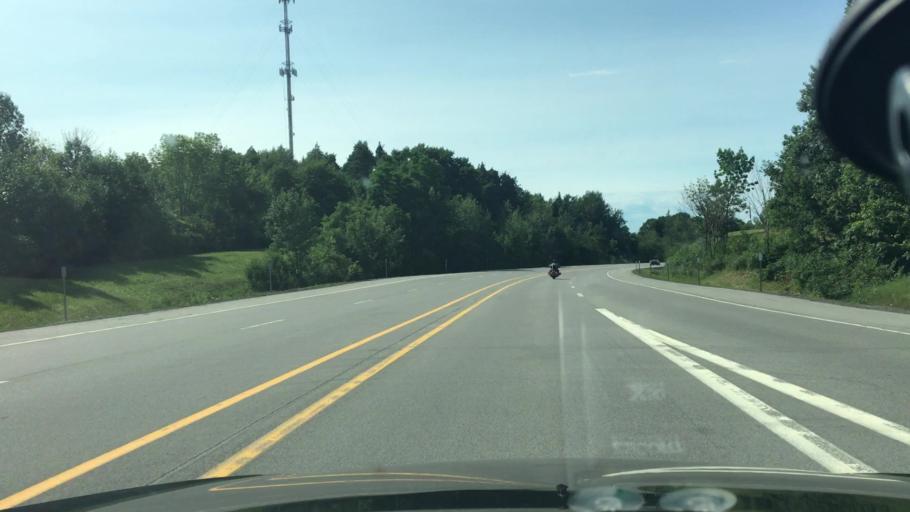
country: US
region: New York
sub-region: Chautauqua County
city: Silver Creek
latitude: 42.5530
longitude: -79.1104
